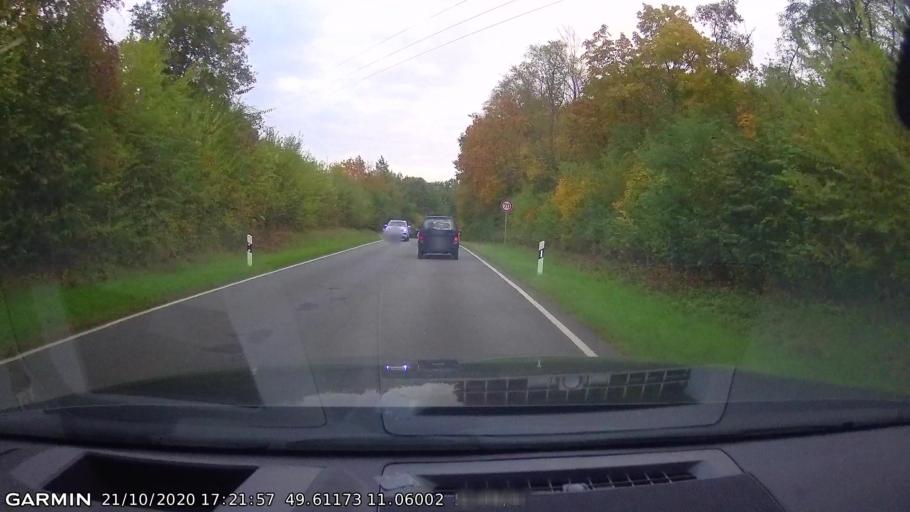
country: DE
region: Bavaria
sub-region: Regierungsbezirk Mittelfranken
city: Spardorf
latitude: 49.6119
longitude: 11.0599
